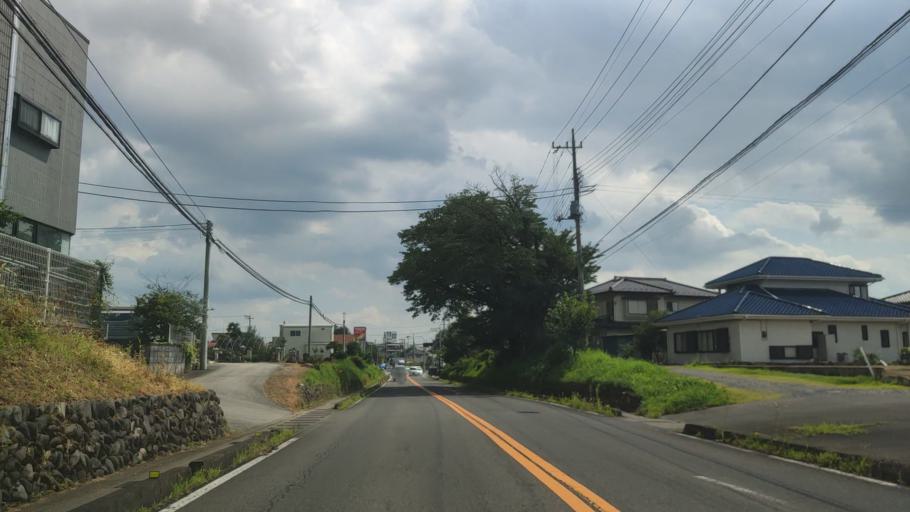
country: JP
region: Tochigi
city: Utsunomiya-shi
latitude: 36.6088
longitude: 139.8566
